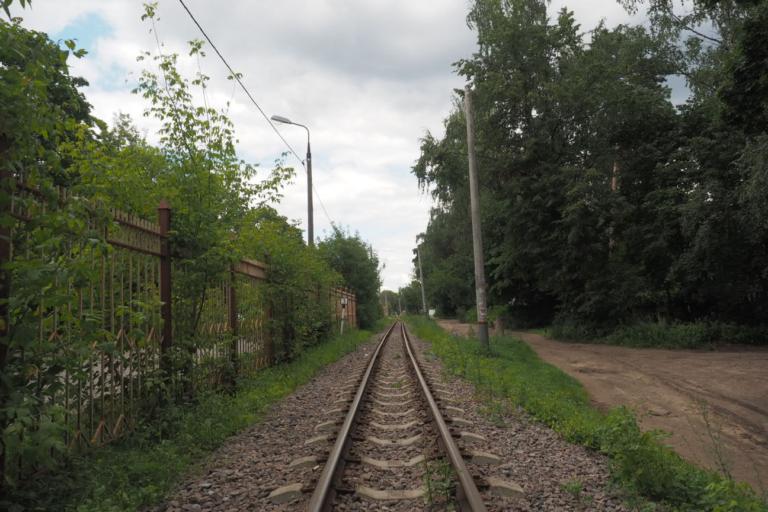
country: RU
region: Moskovskaya
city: Zhukovskiy
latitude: 55.5852
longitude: 38.1416
